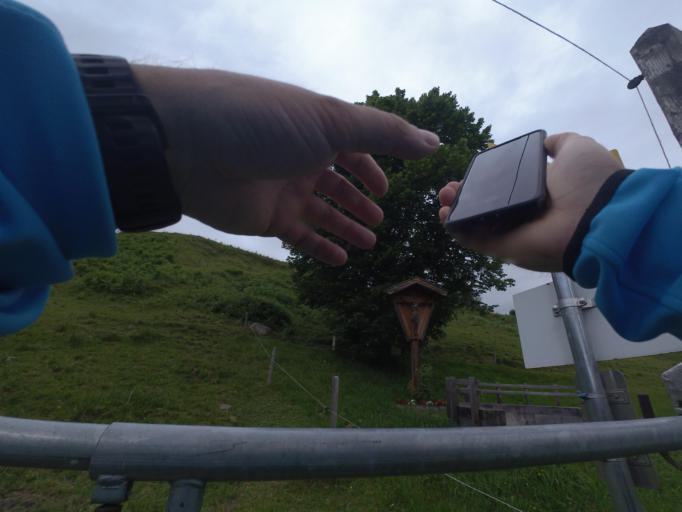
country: AT
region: Salzburg
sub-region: Politischer Bezirk Zell am See
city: Leogang
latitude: 47.4351
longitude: 12.7521
